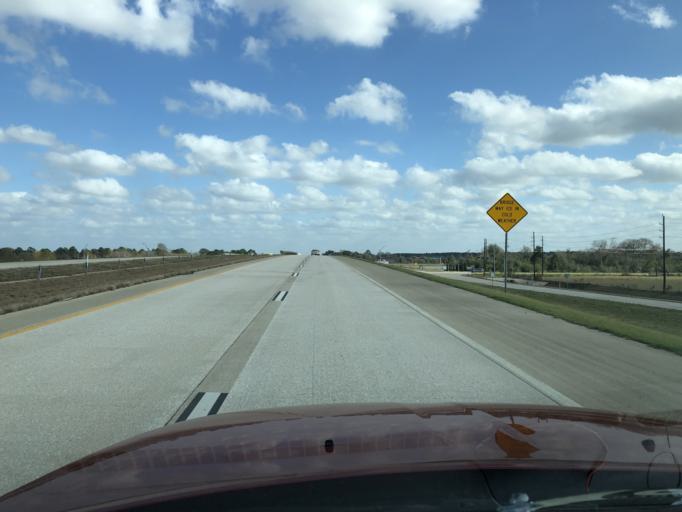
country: US
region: Texas
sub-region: Harris County
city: Cypress
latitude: 30.0527
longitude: -95.6999
